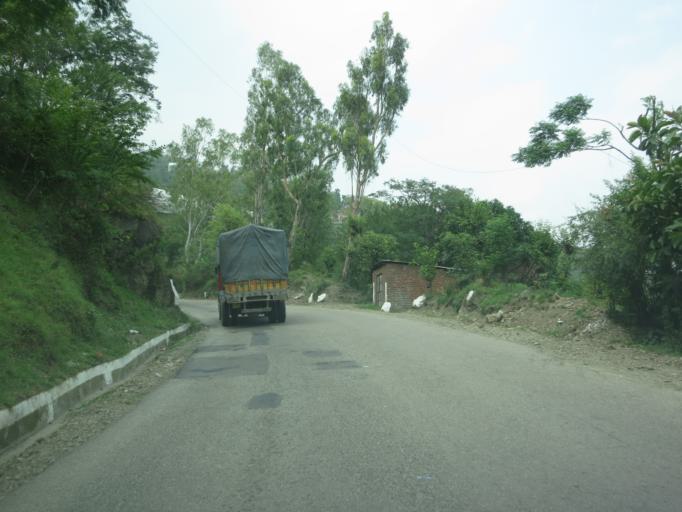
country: IN
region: Himachal Pradesh
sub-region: Bilaspur
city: Bilaspur
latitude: 31.2579
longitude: 76.8663
